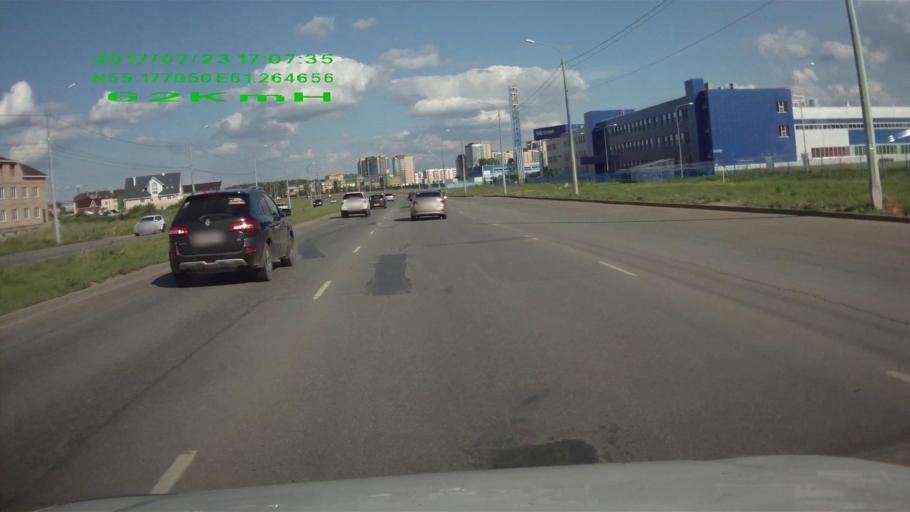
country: RU
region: Chelyabinsk
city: Roshchino
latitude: 55.1768
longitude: 61.2658
